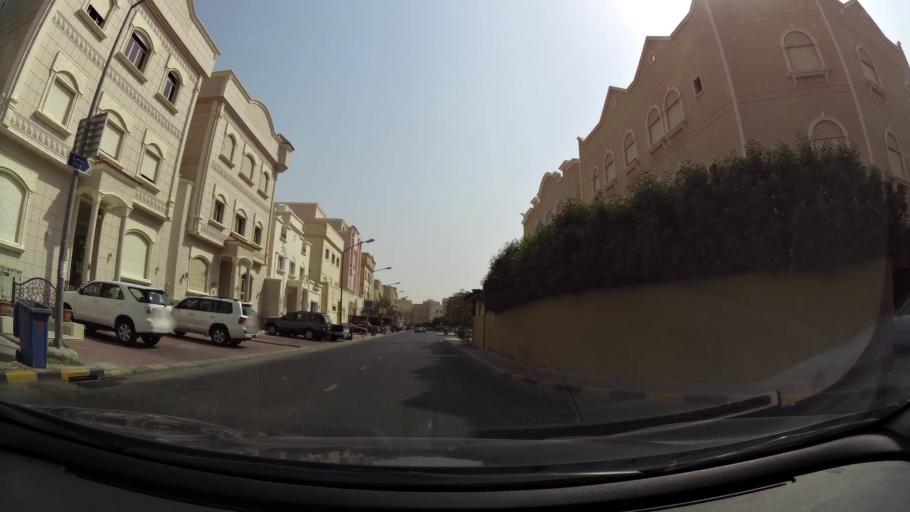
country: KW
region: Muhafazat al Jahra'
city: Al Jahra'
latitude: 29.3220
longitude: 47.7374
